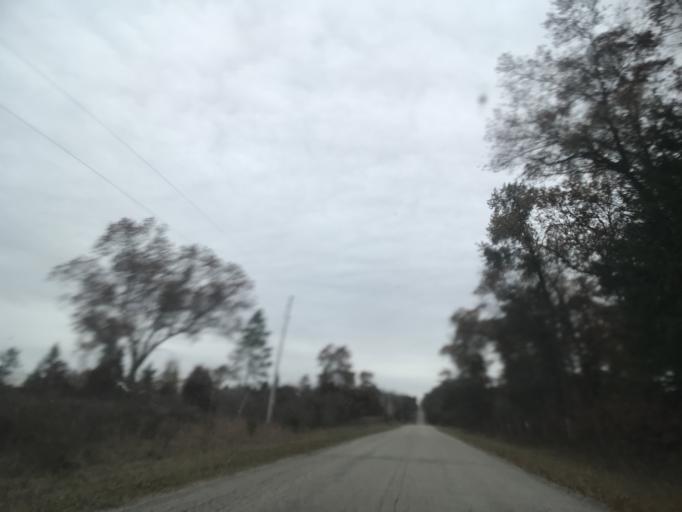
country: US
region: Wisconsin
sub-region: Oconto County
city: Gillett
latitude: 45.3289
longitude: -88.2760
